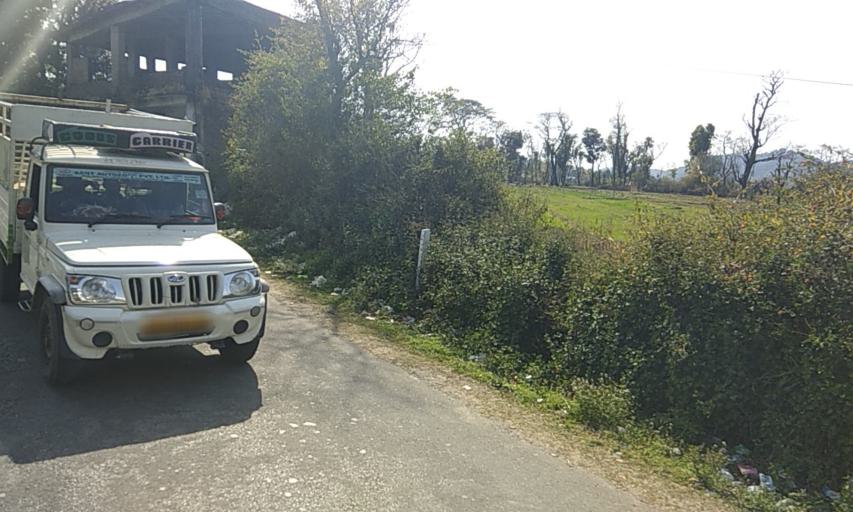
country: IN
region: Himachal Pradesh
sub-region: Kangra
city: Dharmsala
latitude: 32.1524
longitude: 76.4172
